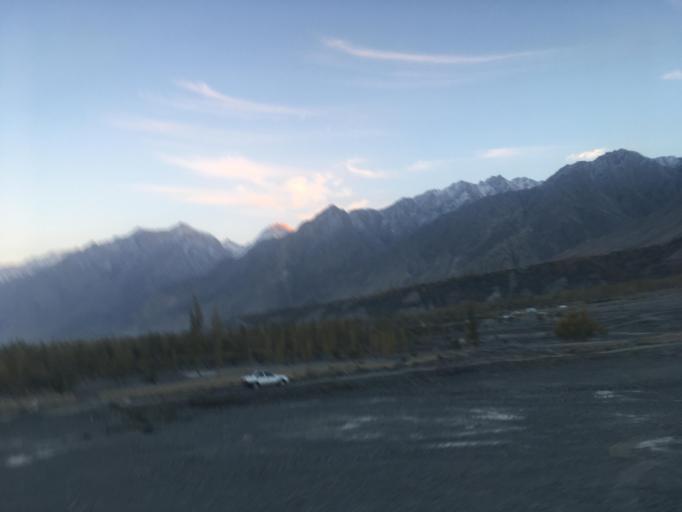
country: PK
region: Gilgit-Baltistan
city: Skardu
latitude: 35.3062
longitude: 75.5383
